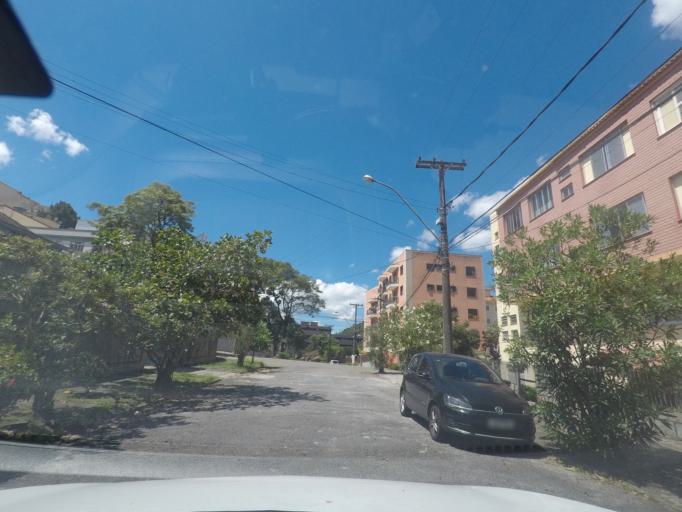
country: BR
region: Rio de Janeiro
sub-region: Teresopolis
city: Teresopolis
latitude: -22.4360
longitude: -42.9776
